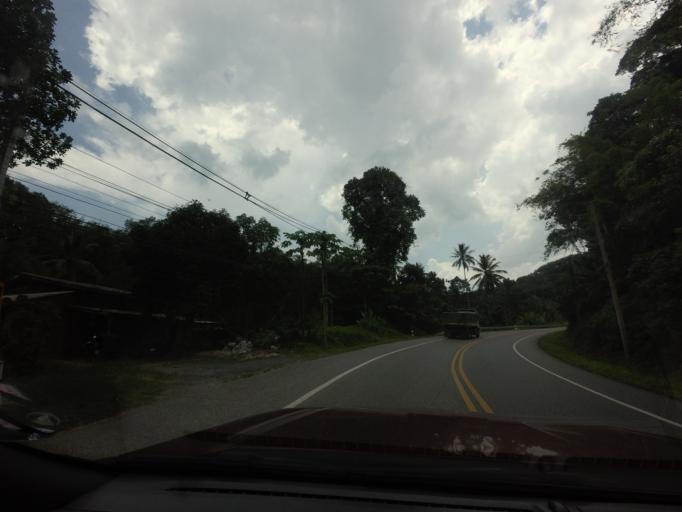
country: TH
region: Yala
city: Than To
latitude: 6.0789
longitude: 101.1866
